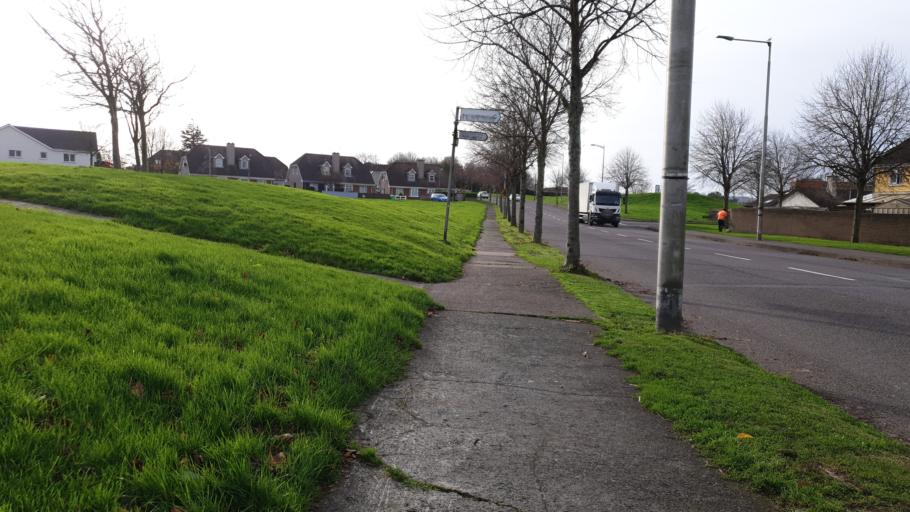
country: IE
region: Munster
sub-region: County Cork
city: Cork
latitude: 51.8935
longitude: -8.4078
